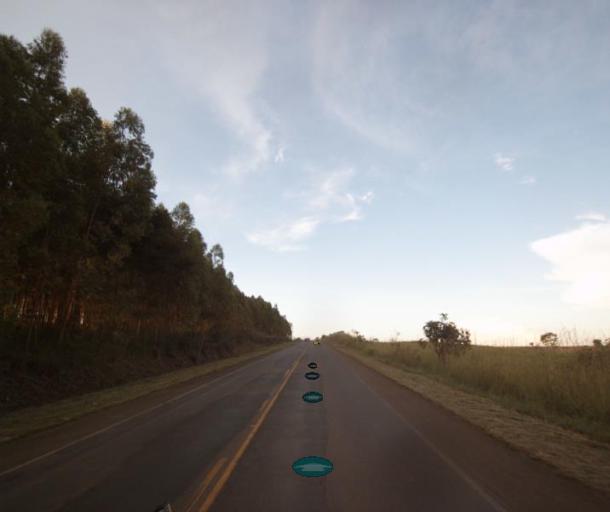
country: BR
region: Goias
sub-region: Abadiania
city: Abadiania
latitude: -16.0946
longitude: -48.8535
